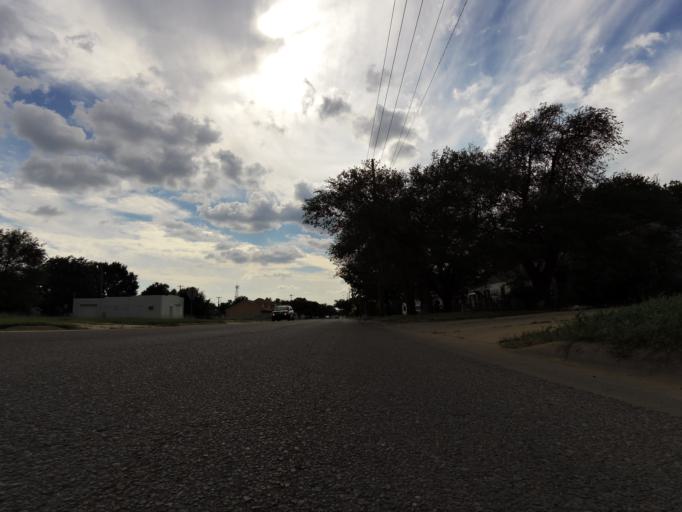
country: US
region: Kansas
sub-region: Sedgwick County
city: Wichita
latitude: 37.7010
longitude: -97.3085
